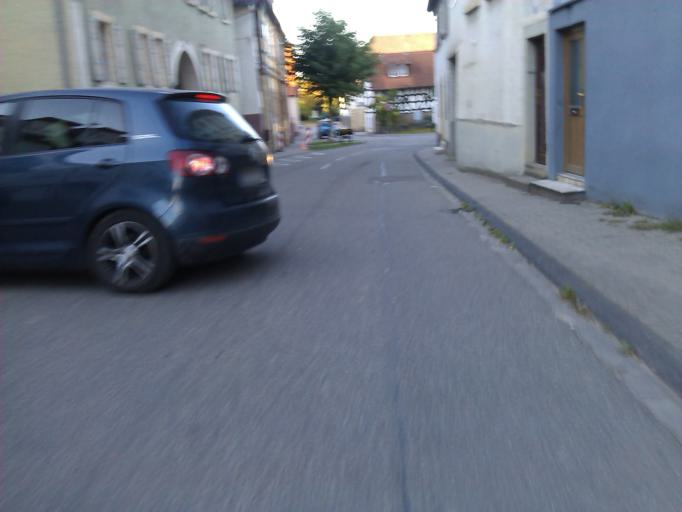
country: DE
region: Baden-Wuerttemberg
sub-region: Regierungsbezirk Stuttgart
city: Ittlingen
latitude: 49.1926
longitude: 8.9336
